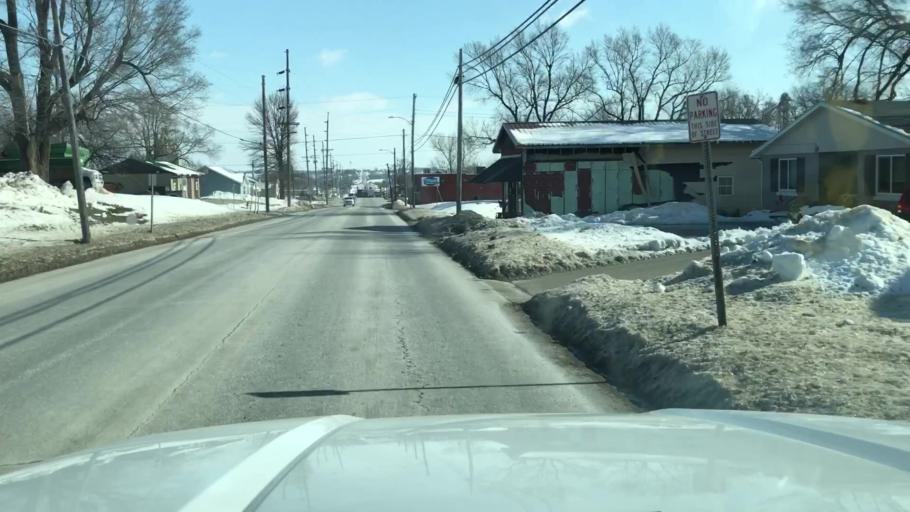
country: US
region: Missouri
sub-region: Nodaway County
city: Maryville
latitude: 40.3454
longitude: -94.8585
